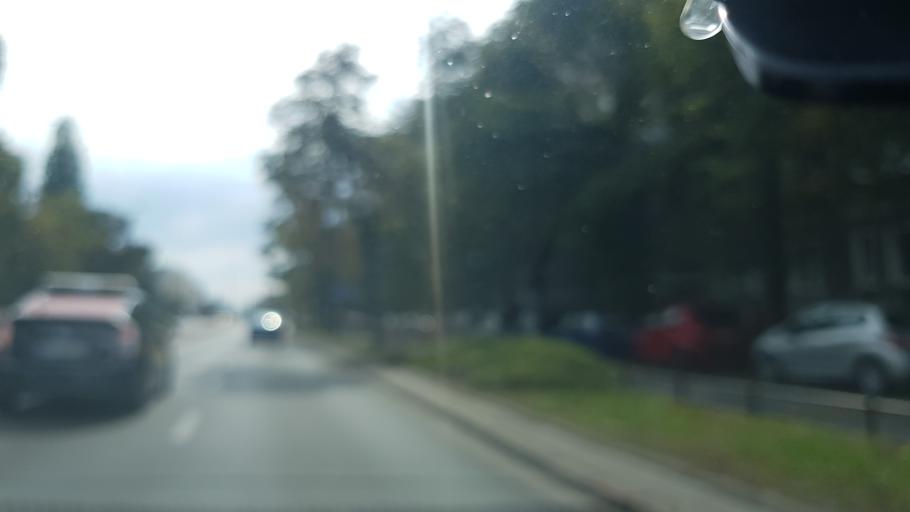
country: PL
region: Masovian Voivodeship
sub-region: Warszawa
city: Mokotow
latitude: 52.2022
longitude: 21.0106
